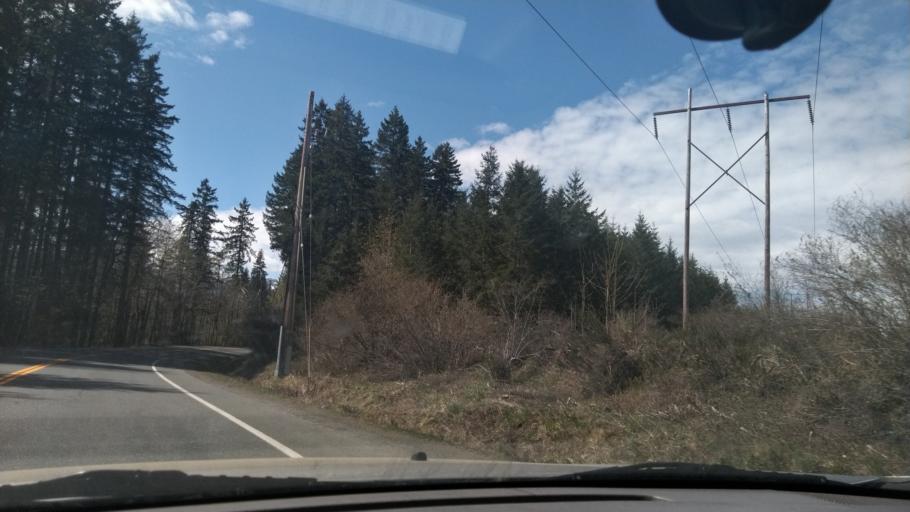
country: CA
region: British Columbia
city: Courtenay
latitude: 49.6959
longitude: -125.0620
